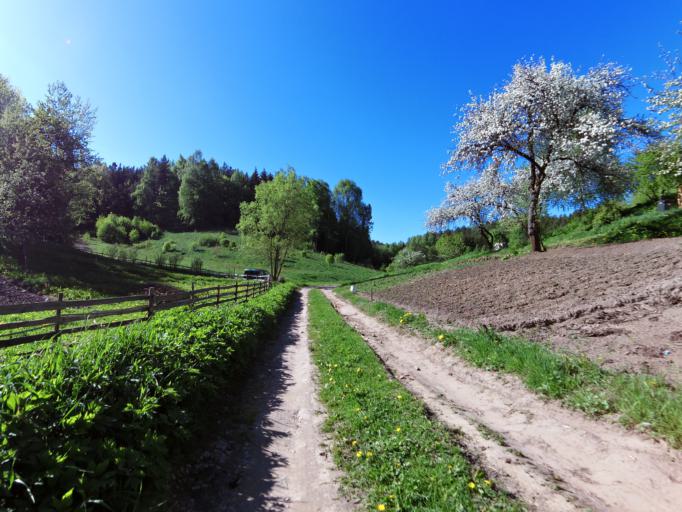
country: LT
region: Vilnius County
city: Pilaite
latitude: 54.6859
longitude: 25.1508
